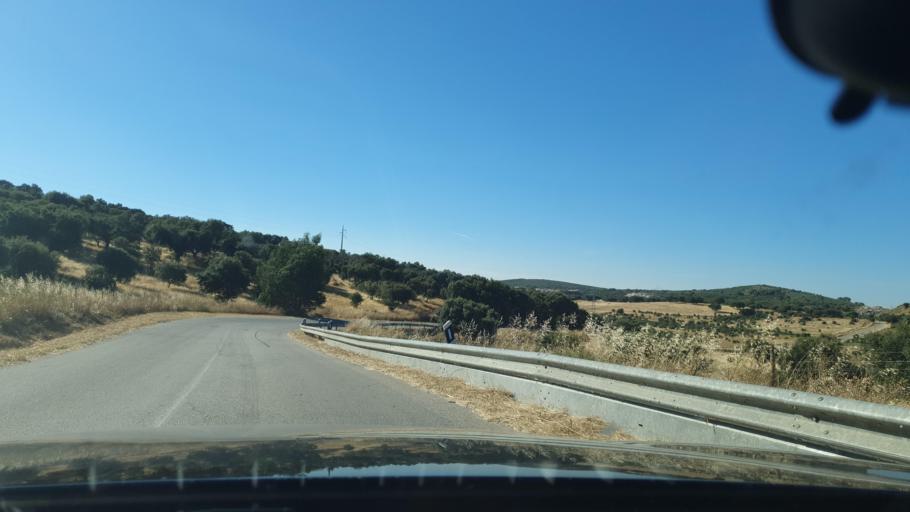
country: PT
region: Evora
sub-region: Alandroal
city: Alandroal
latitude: 38.7282
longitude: -7.4049
